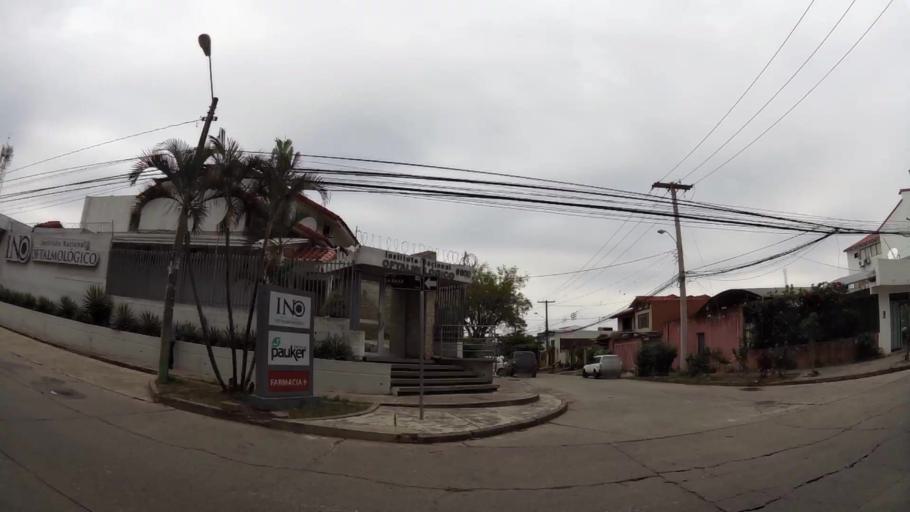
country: BO
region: Santa Cruz
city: Santa Cruz de la Sierra
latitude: -17.7634
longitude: -63.1911
